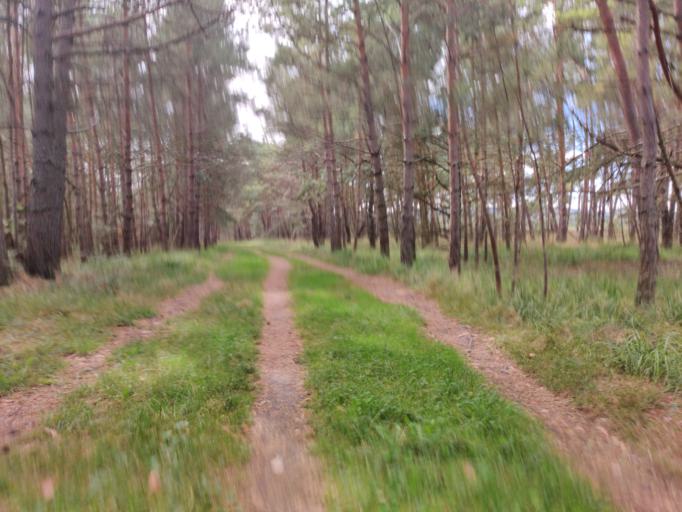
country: DE
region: Lower Saxony
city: Langelsheim
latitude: 51.9620
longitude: 10.3557
